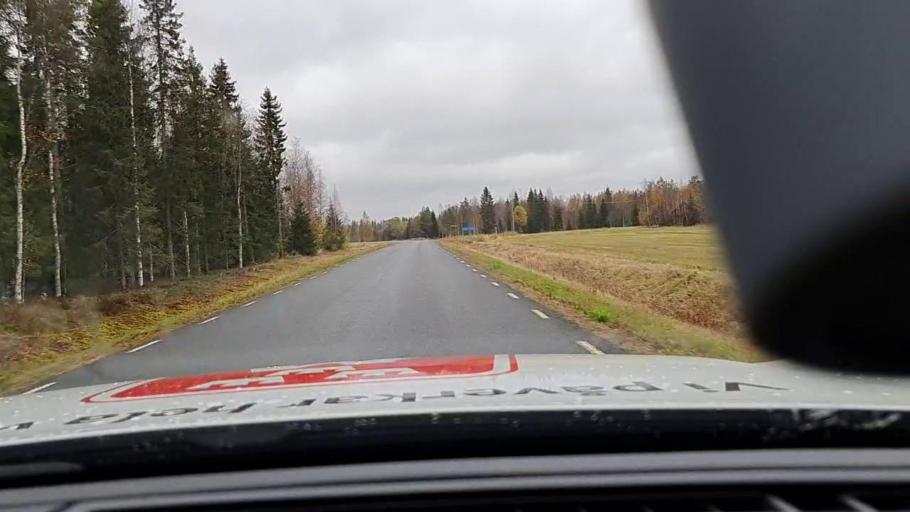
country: SE
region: Norrbotten
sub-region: Haparanda Kommun
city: Haparanda
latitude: 65.9313
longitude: 23.8160
